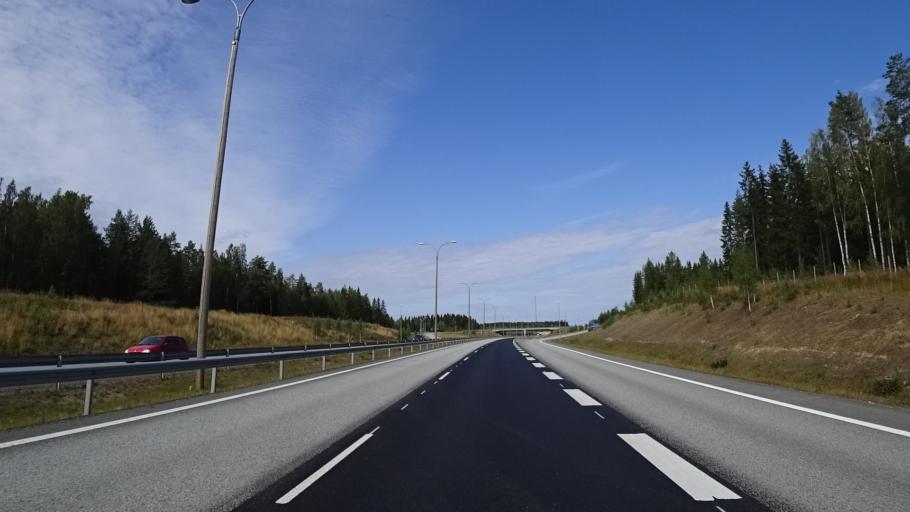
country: FI
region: North Karelia
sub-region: Joensuu
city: Joensuu
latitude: 62.5627
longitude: 29.8352
